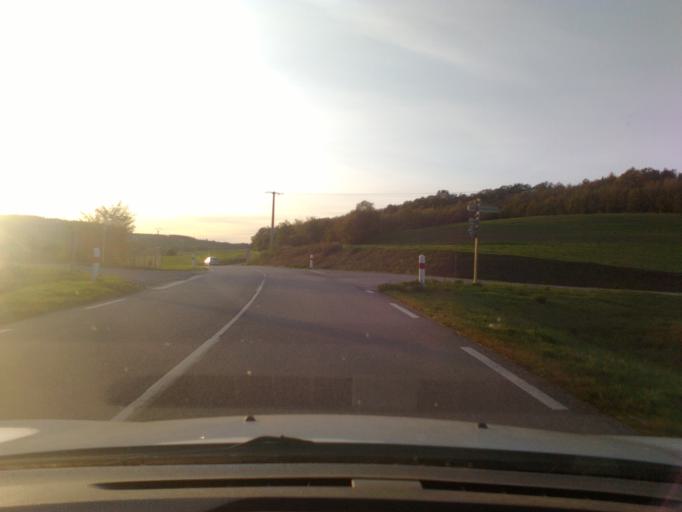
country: FR
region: Lorraine
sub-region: Departement des Vosges
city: Vincey
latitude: 48.3459
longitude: 6.3035
